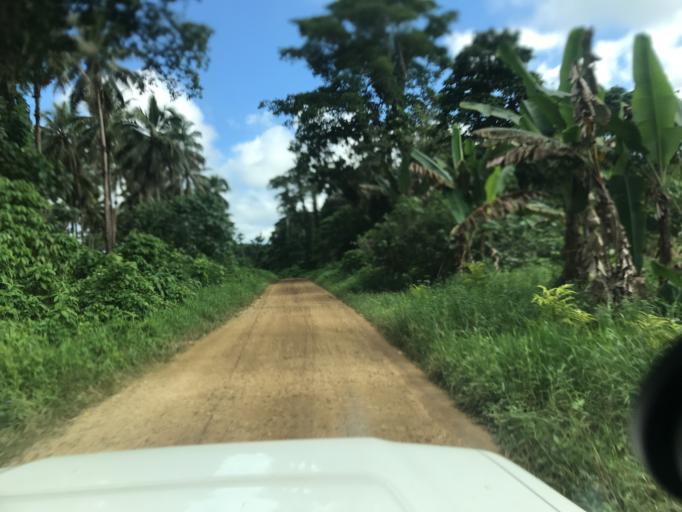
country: VU
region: Sanma
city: Luganville
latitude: -15.4738
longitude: 167.0827
